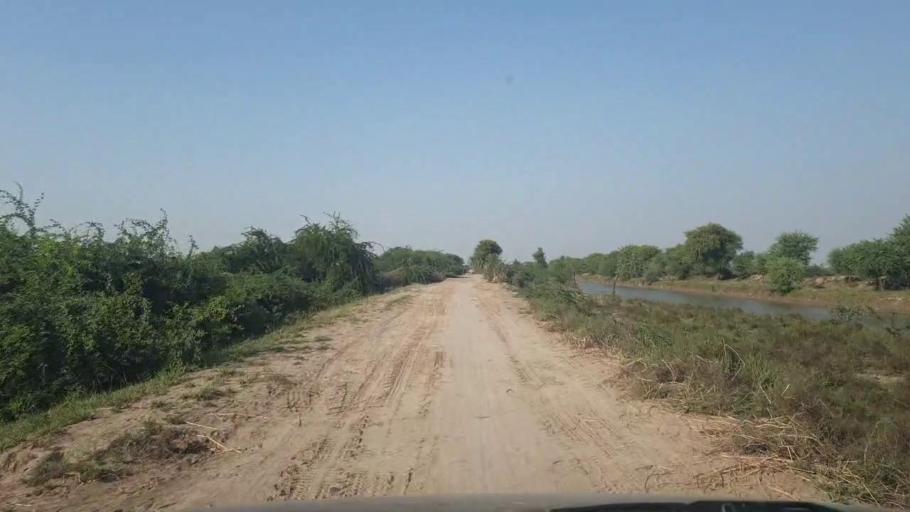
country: PK
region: Sindh
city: Badin
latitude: 24.6314
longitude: 68.8149
